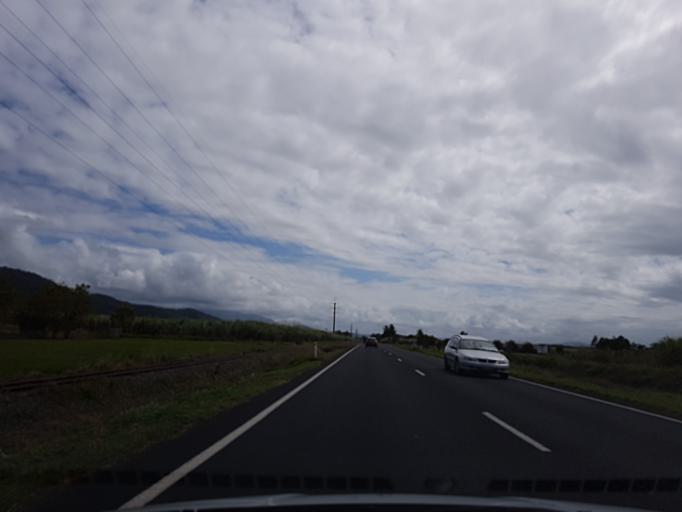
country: AU
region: Queensland
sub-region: Cairns
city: Port Douglas
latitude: -16.5180
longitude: 145.4486
